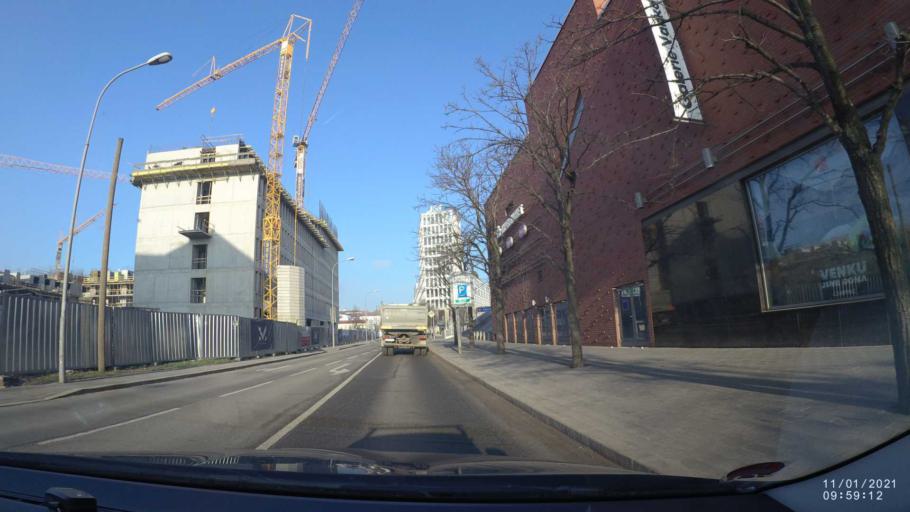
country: CZ
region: South Moravian
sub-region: Mesto Brno
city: Brno
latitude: 49.1865
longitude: 16.6147
